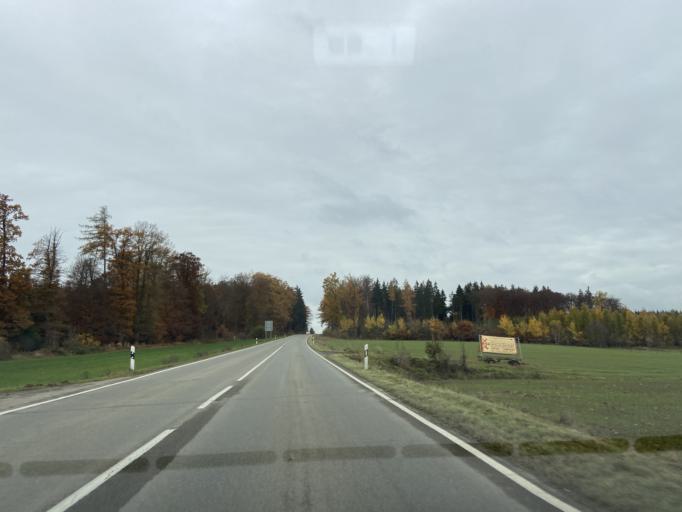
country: DE
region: Baden-Wuerttemberg
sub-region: Tuebingen Region
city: Wald
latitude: 47.9694
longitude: 9.1530
